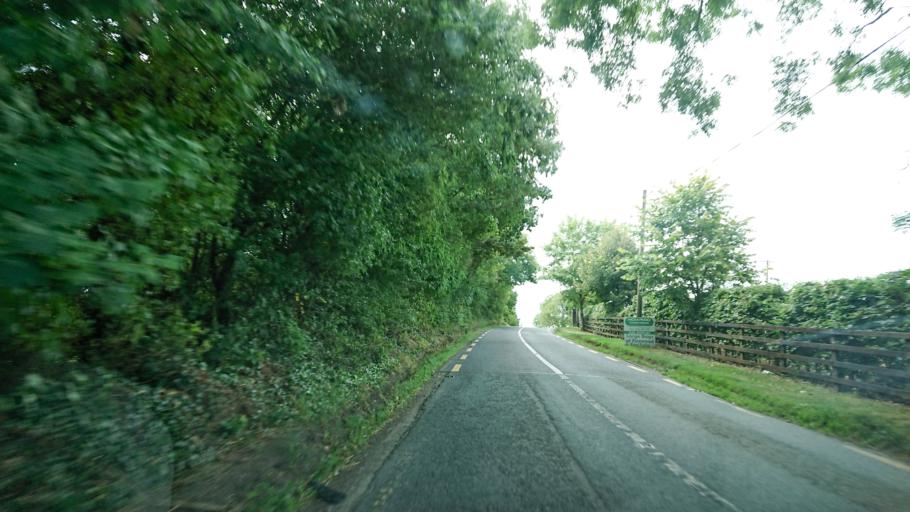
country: IE
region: Munster
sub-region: County Cork
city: Mallow
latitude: 52.1527
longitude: -8.5349
